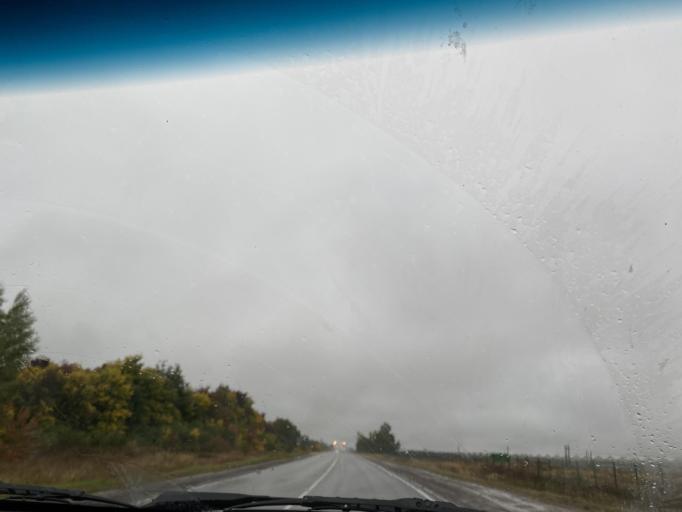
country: RU
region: Rjazan
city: Ryazan'
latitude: 54.4699
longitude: 39.8575
